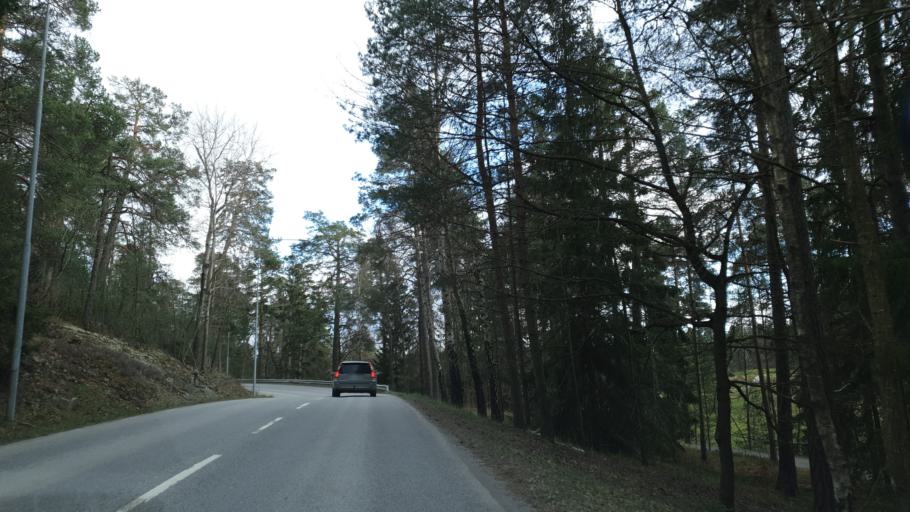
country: SE
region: Stockholm
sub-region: Lidingo
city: Lidingoe
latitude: 59.3809
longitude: 18.1228
